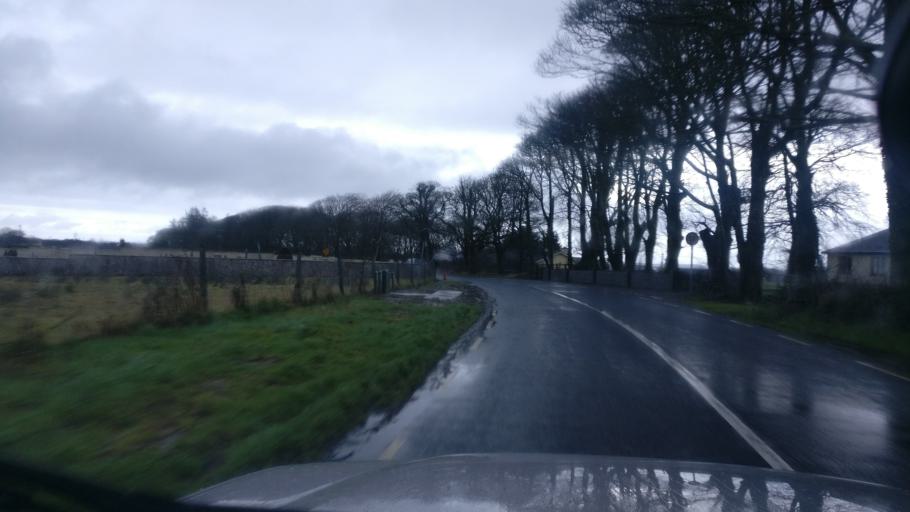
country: IE
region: Connaught
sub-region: County Galway
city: Ballinasloe
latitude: 53.3243
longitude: -8.4069
